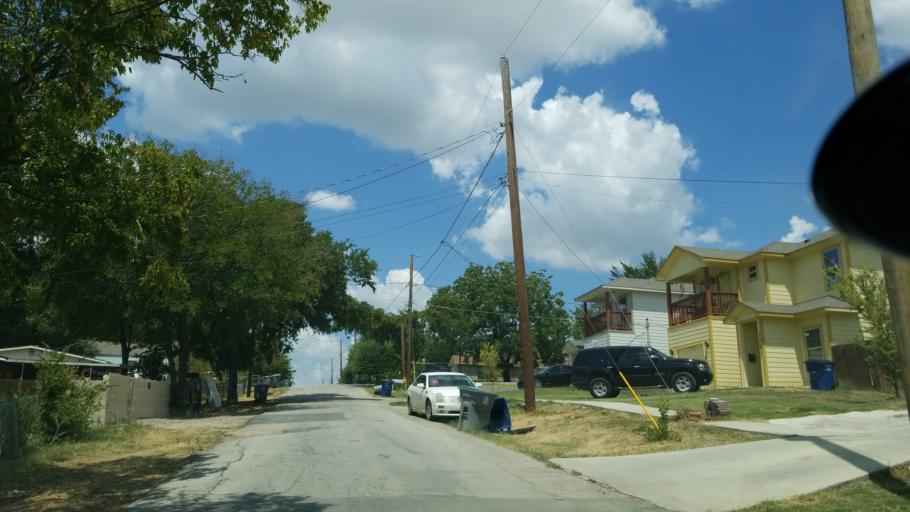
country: US
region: Texas
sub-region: Dallas County
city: Cockrell Hill
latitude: 32.7435
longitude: -96.9114
